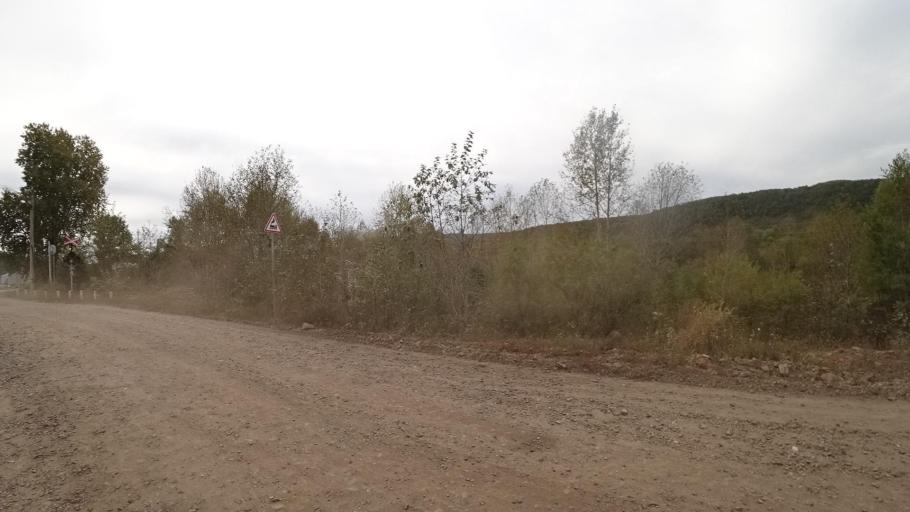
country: RU
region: Jewish Autonomous Oblast
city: Khingansk
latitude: 49.0213
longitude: 131.0543
